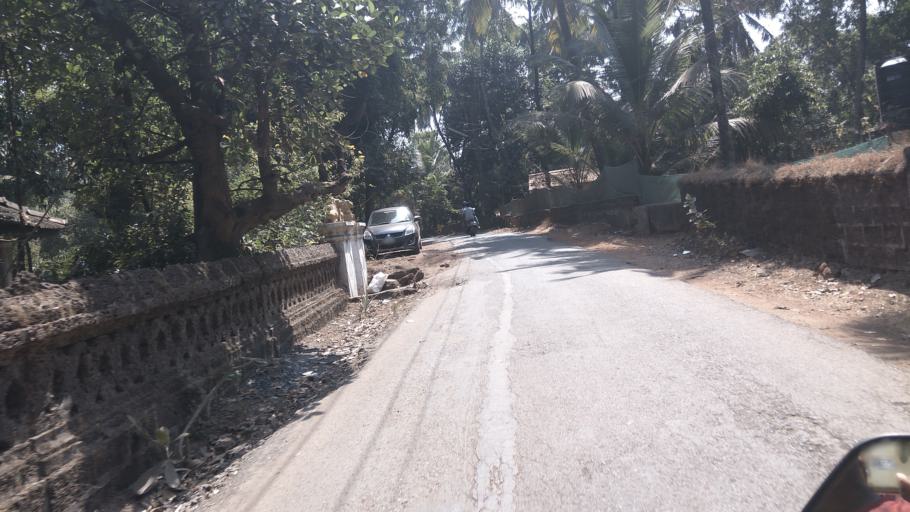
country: IN
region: Goa
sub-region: North Goa
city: Vagator
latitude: 15.6007
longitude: 73.7396
